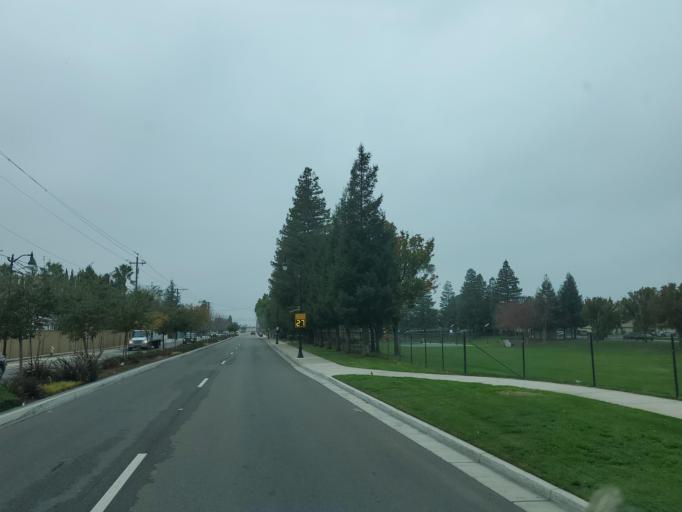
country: US
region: California
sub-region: San Joaquin County
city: Lathrop
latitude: 37.8264
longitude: -121.2794
